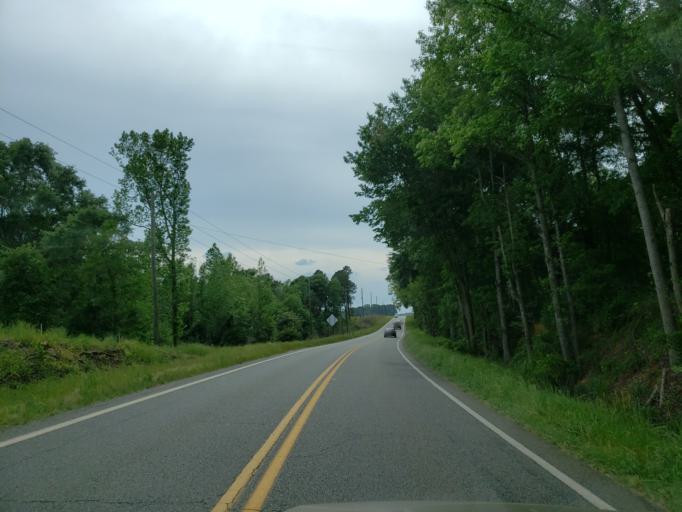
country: US
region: Georgia
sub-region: Macon County
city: Marshallville
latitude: 32.3664
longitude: -83.9054
